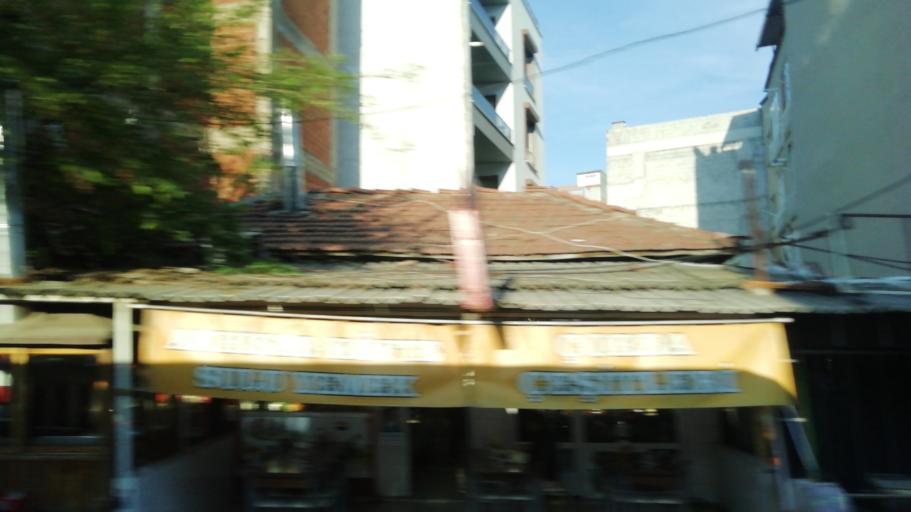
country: TR
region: Manisa
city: Akhisar
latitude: 38.9274
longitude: 27.8344
